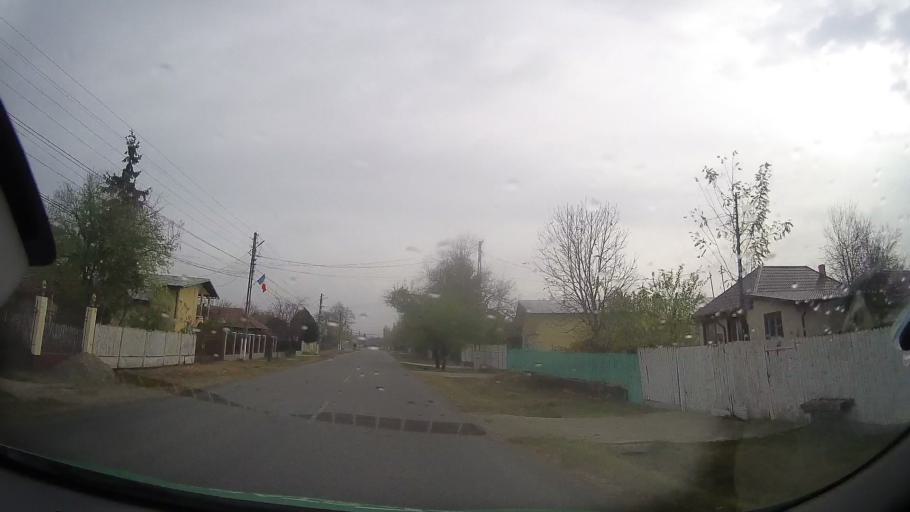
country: RO
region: Prahova
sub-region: Comuna Rafov
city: Palanca
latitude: 44.8452
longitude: 26.2321
